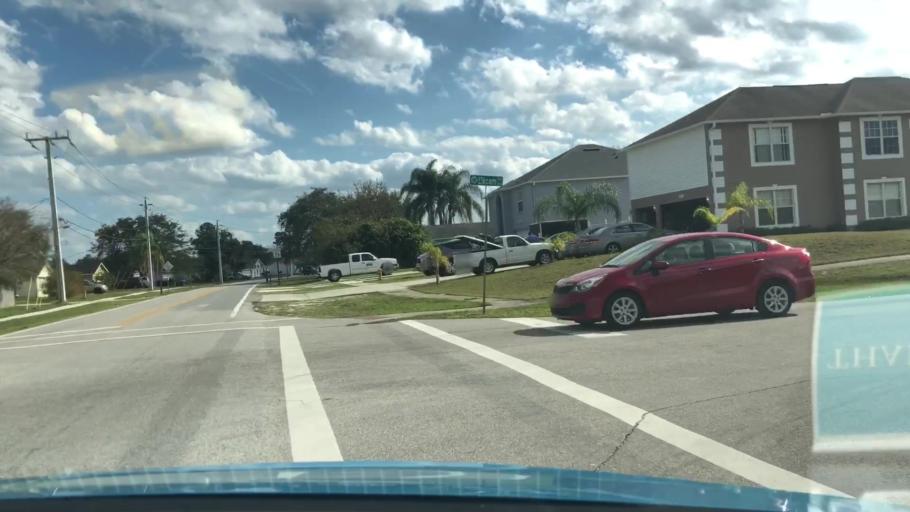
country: US
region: Florida
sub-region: Volusia County
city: Lake Helen
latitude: 28.9336
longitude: -81.1775
